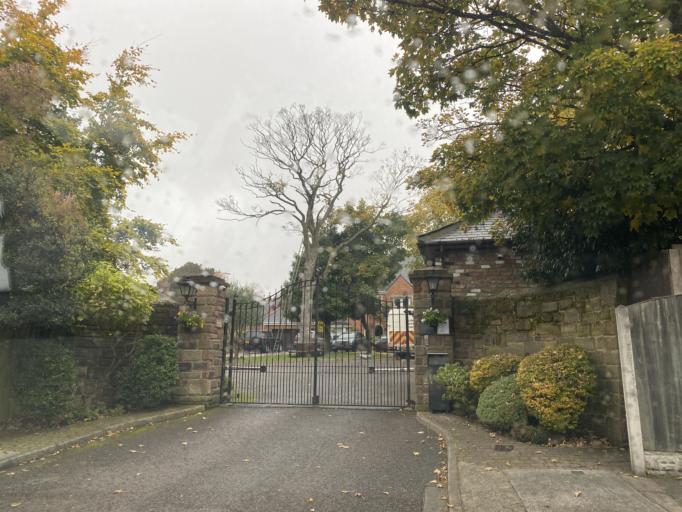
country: GB
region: England
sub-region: Knowsley
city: Huyton
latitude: 53.3794
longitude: -2.8806
